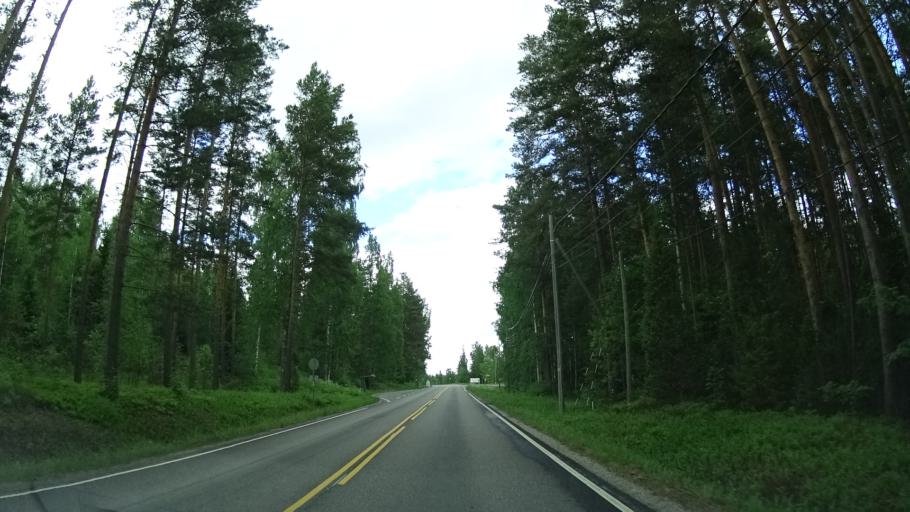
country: FI
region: Paijanne Tavastia
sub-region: Lahti
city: Asikkala
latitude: 61.3300
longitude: 25.5714
